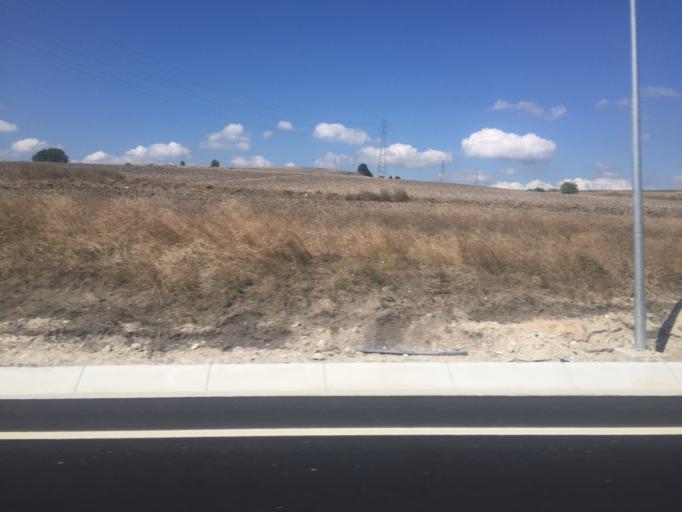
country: TR
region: Balikesir
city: Susurluk
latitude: 39.9651
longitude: 28.1640
